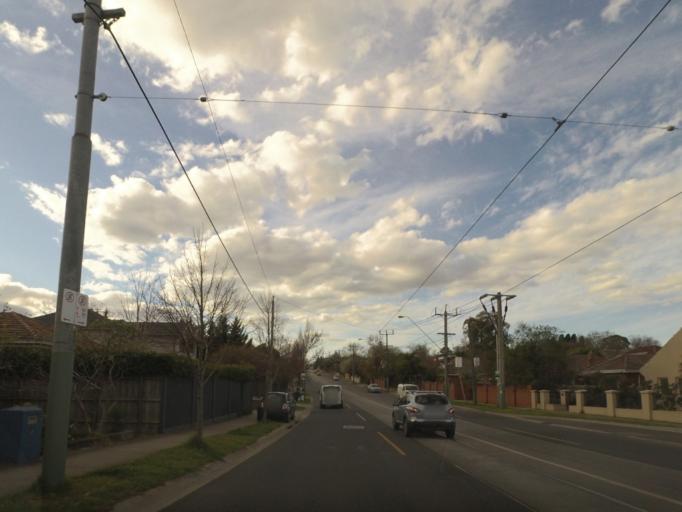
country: AU
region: Victoria
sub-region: Stonnington
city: Glen Iris
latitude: -37.8501
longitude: 145.0529
